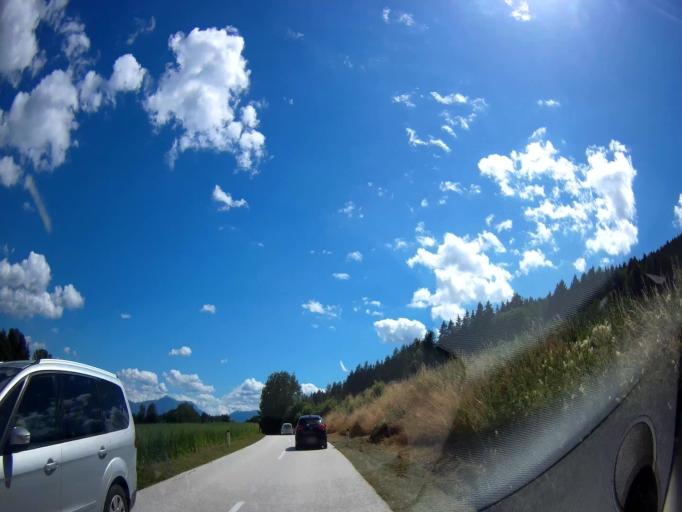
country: AT
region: Carinthia
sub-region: Politischer Bezirk Sankt Veit an der Glan
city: St. Georgen am Laengsee
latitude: 46.7208
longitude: 14.4157
